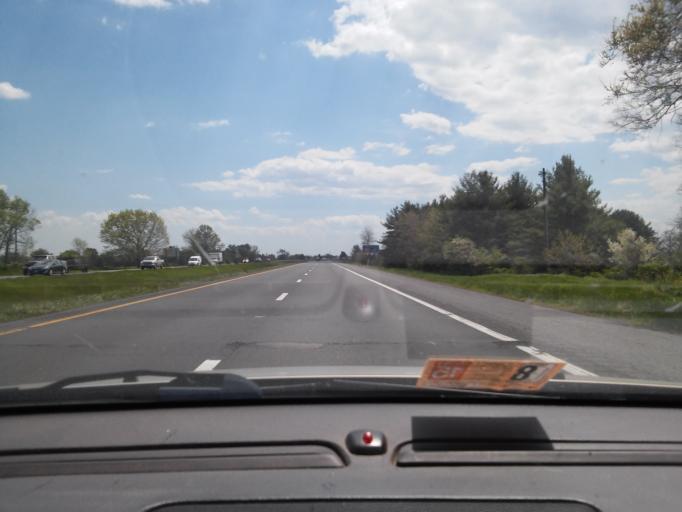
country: US
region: West Virginia
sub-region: Berkeley County
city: Inwood
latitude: 39.3038
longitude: -78.0793
